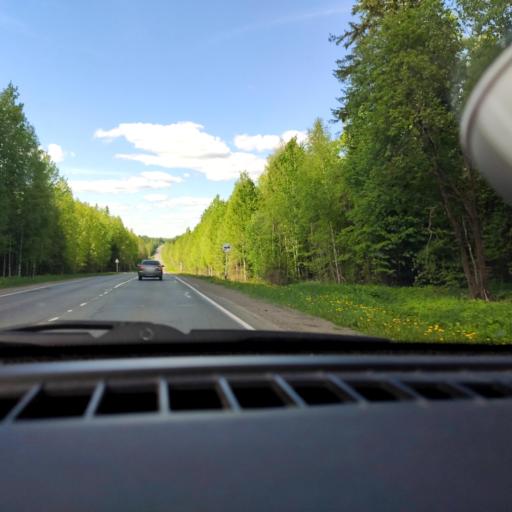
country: RU
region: Perm
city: Perm
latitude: 58.2266
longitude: 56.1636
